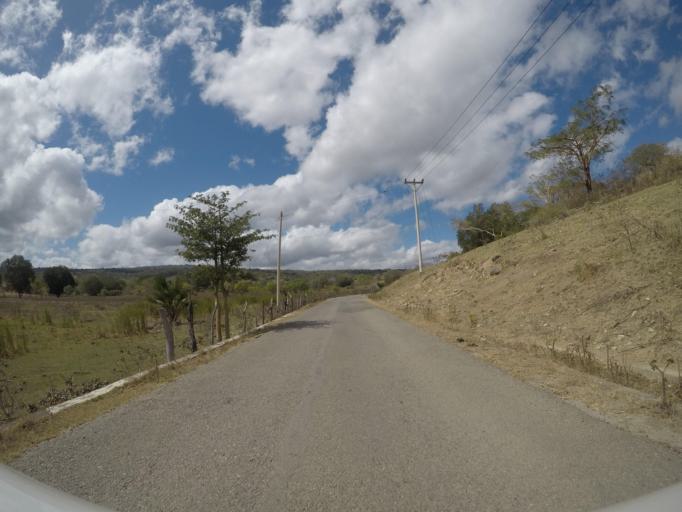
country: TL
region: Lautem
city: Lospalos
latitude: -8.4257
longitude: 126.8311
